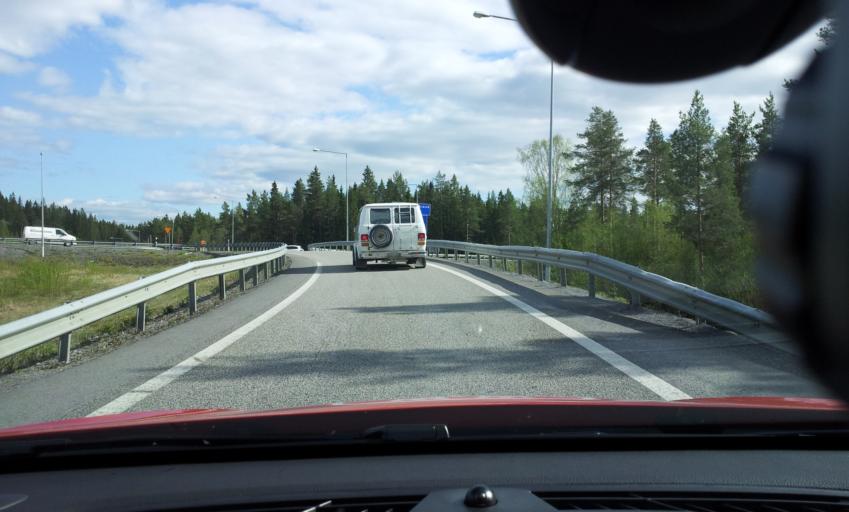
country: SE
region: Jaemtland
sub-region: OEstersunds Kommun
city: Ostersund
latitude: 63.2032
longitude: 14.6756
